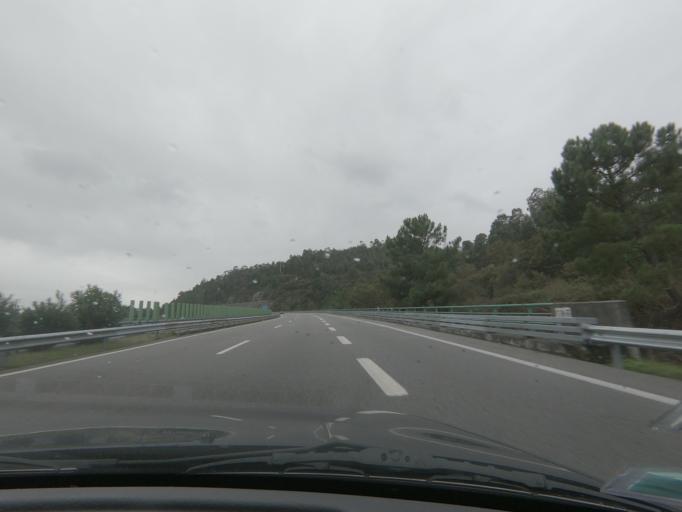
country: PT
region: Porto
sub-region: Marco de Canaveses
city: Marco de Canavezes
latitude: 41.2330
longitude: -8.1244
